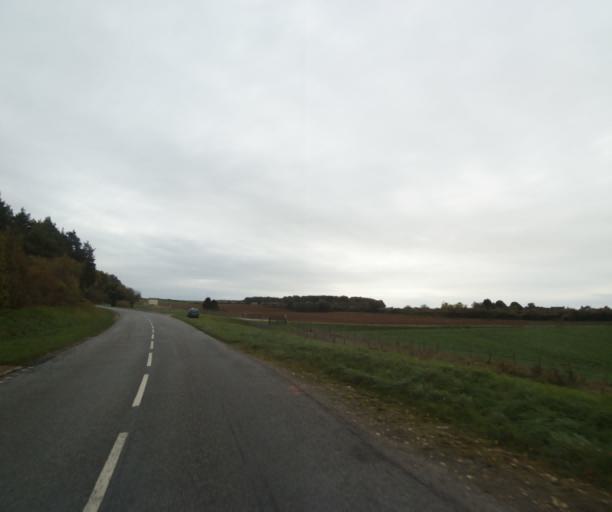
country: FR
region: Centre
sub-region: Departement d'Eure-et-Loir
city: Vert-en-Drouais
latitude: 48.7540
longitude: 1.3098
